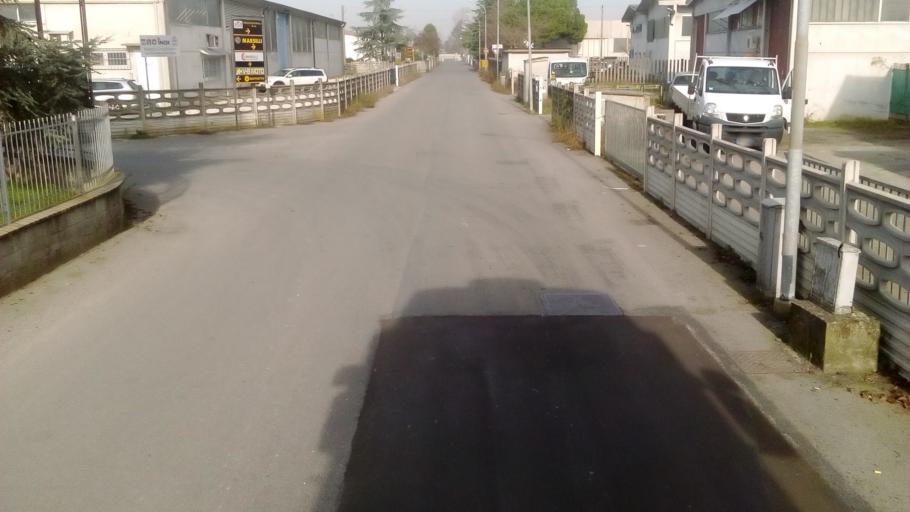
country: IT
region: Lombardy
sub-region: Provincia di Cremona
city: Castelleone
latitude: 45.2938
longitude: 9.7502
